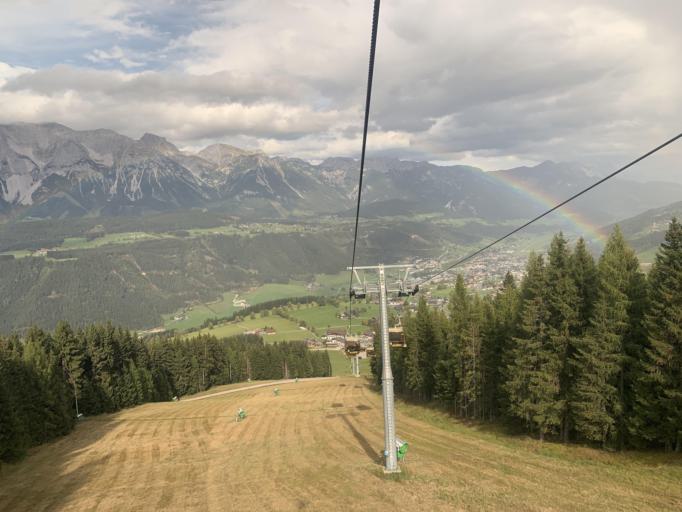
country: AT
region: Styria
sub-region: Politischer Bezirk Liezen
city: Schladming
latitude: 47.3697
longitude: 13.6480
